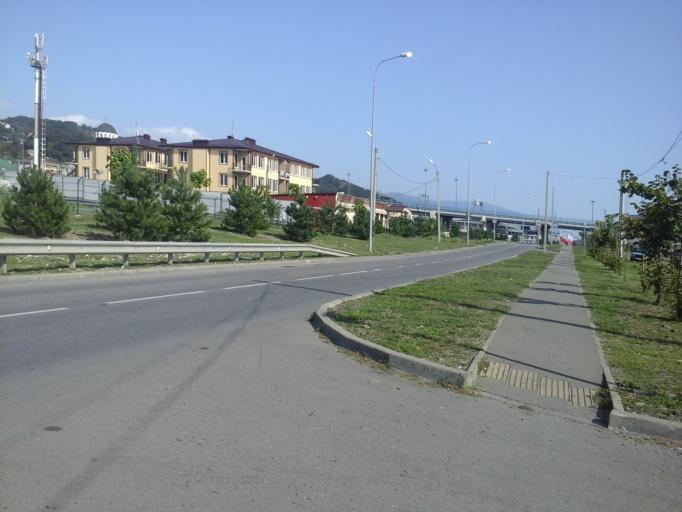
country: RU
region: Krasnodarskiy
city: Adler
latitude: 43.4145
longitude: 39.9645
